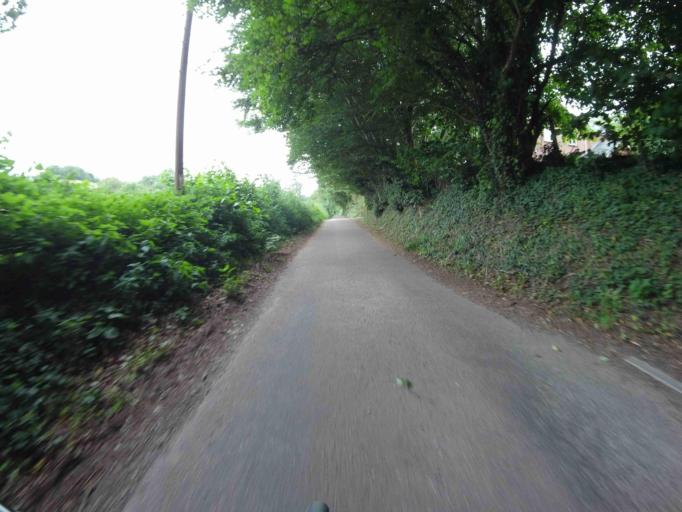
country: GB
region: England
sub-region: Devon
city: Heavitree
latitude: 50.7117
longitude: -3.4906
